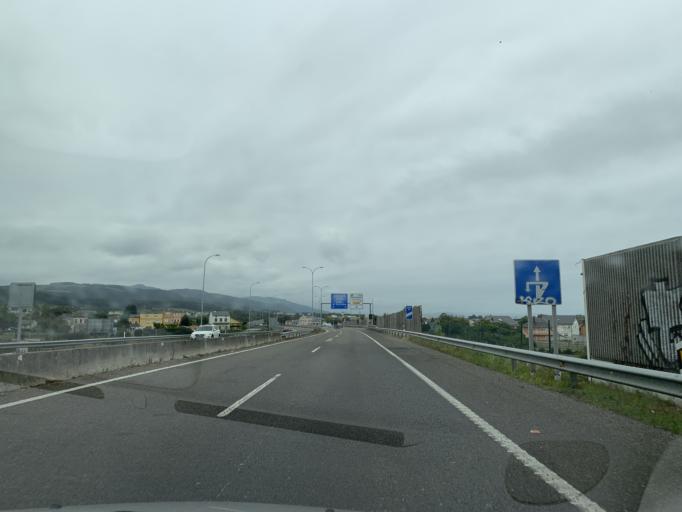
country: ES
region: Galicia
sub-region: Provincia de Lugo
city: Ribadeo
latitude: 43.5430
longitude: -7.0403
